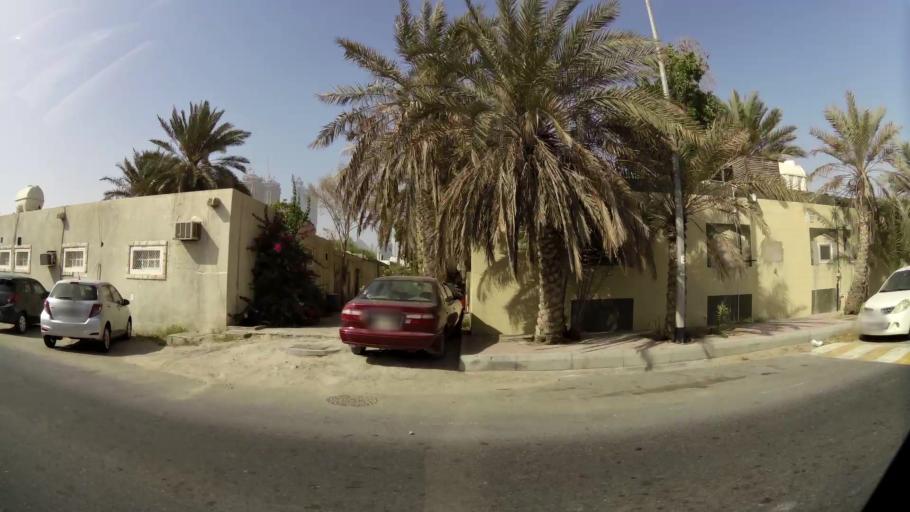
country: AE
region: Dubai
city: Dubai
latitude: 25.1747
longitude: 55.2538
